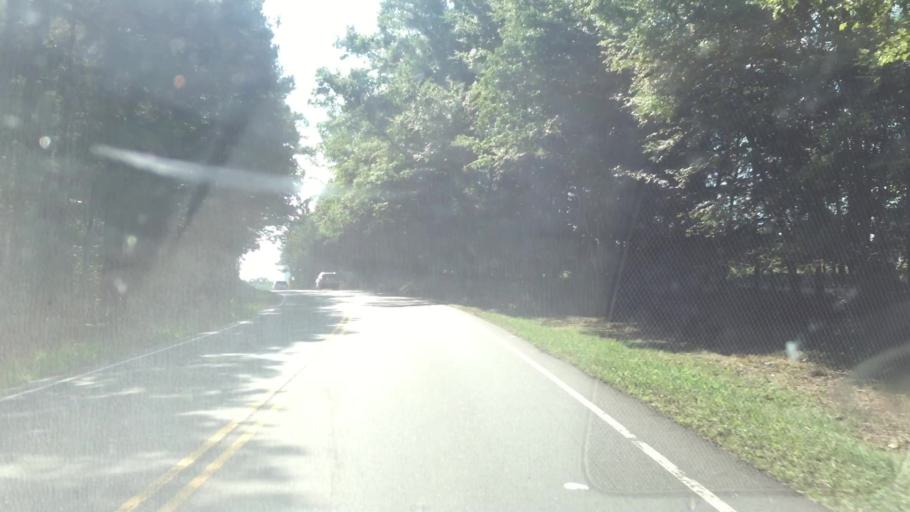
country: US
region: North Carolina
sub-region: Mecklenburg County
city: Mint Hill
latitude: 35.1688
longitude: -80.6001
